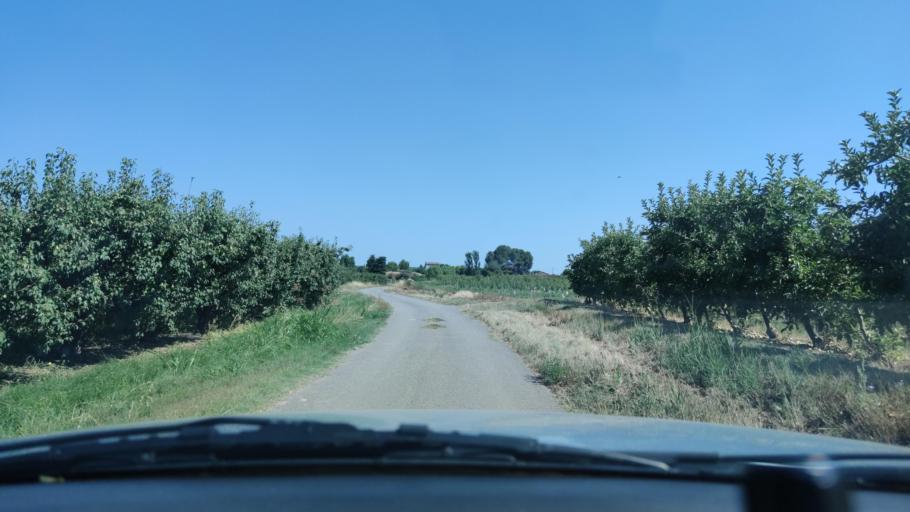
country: ES
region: Catalonia
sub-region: Provincia de Lleida
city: Alcoletge
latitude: 41.6693
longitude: 0.6607
